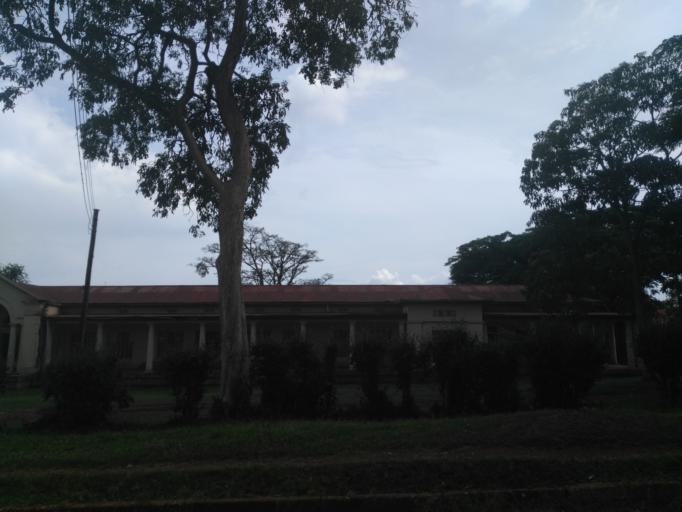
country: UG
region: Eastern Region
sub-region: Jinja District
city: Jinja
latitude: 0.4218
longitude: 33.2058
